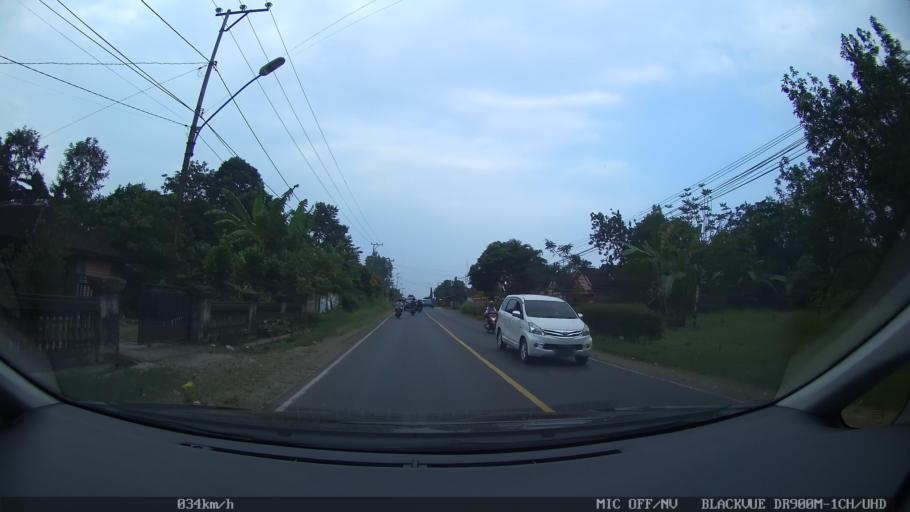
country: ID
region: Lampung
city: Gedongtataan
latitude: -5.3676
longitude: 105.1398
